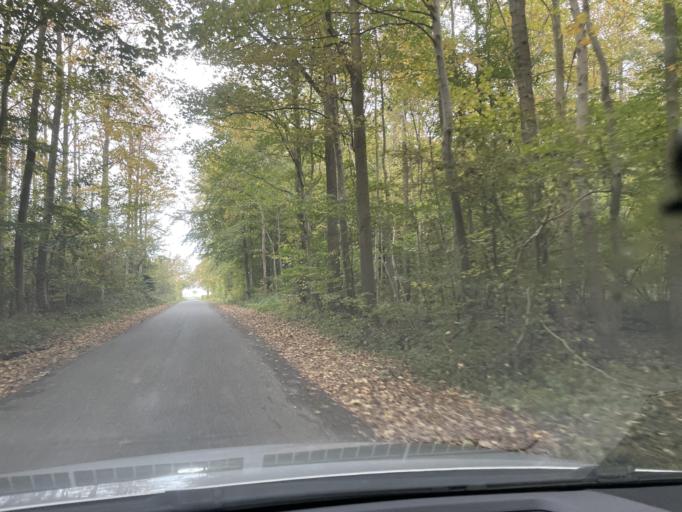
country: DK
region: South Denmark
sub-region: Kerteminde Kommune
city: Kerteminde
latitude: 55.4247
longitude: 10.6907
